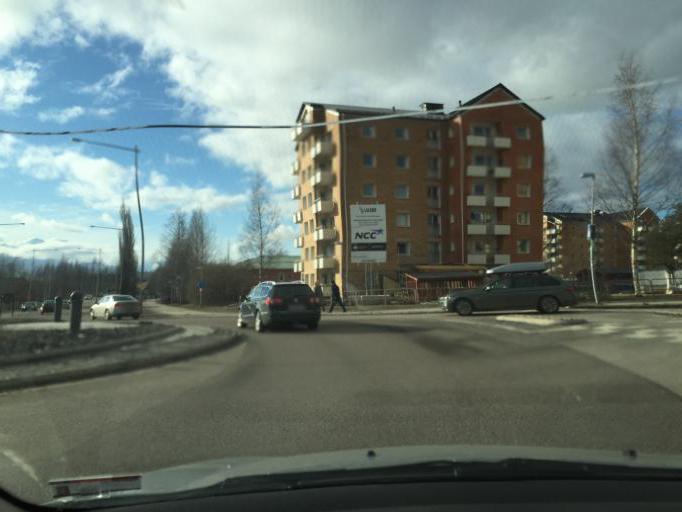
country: SE
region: Norrbotten
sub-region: Lulea Kommun
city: Lulea
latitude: 65.5804
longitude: 22.1758
